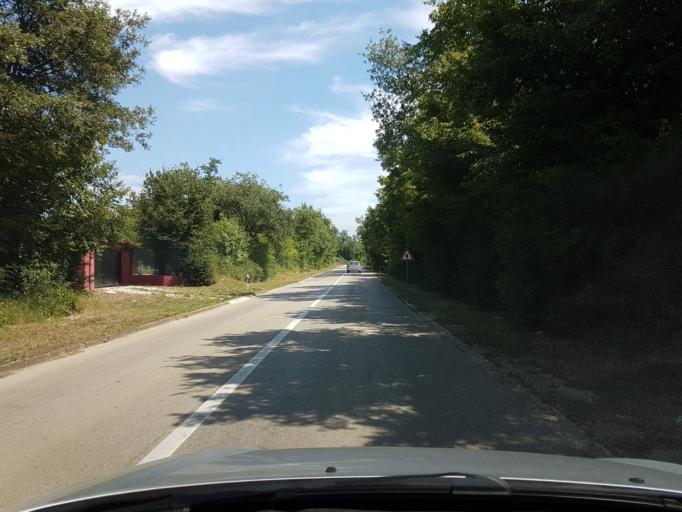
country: HR
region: Istarska
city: Vrsar
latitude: 45.1565
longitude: 13.6923
